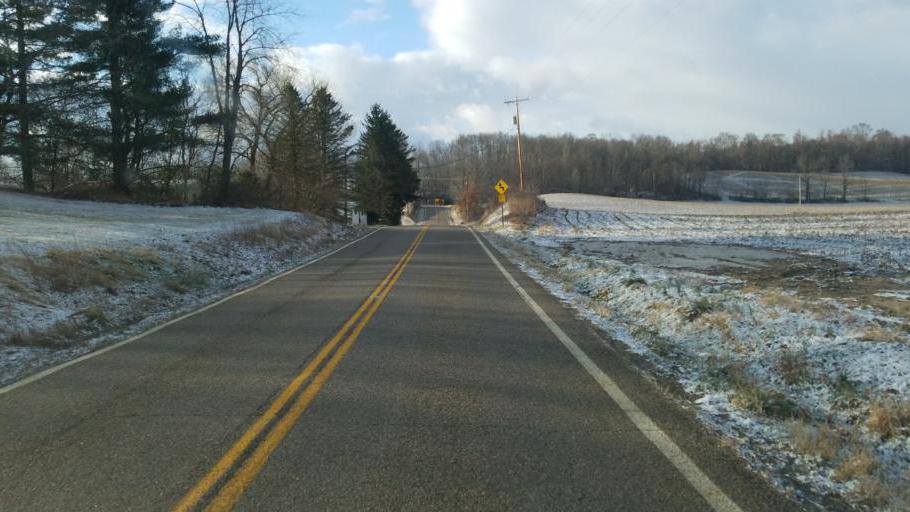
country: US
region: Ohio
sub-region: Ashland County
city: Loudonville
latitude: 40.6456
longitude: -82.1354
